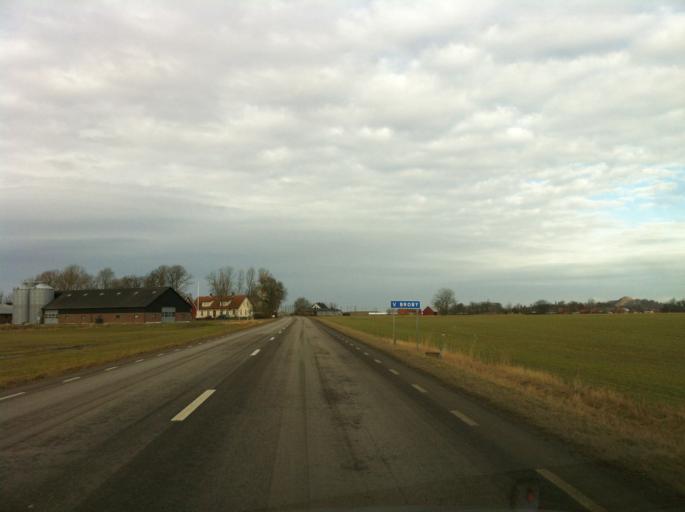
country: SE
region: Skane
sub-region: Bjuvs Kommun
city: Bjuv
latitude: 56.1106
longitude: 12.8939
